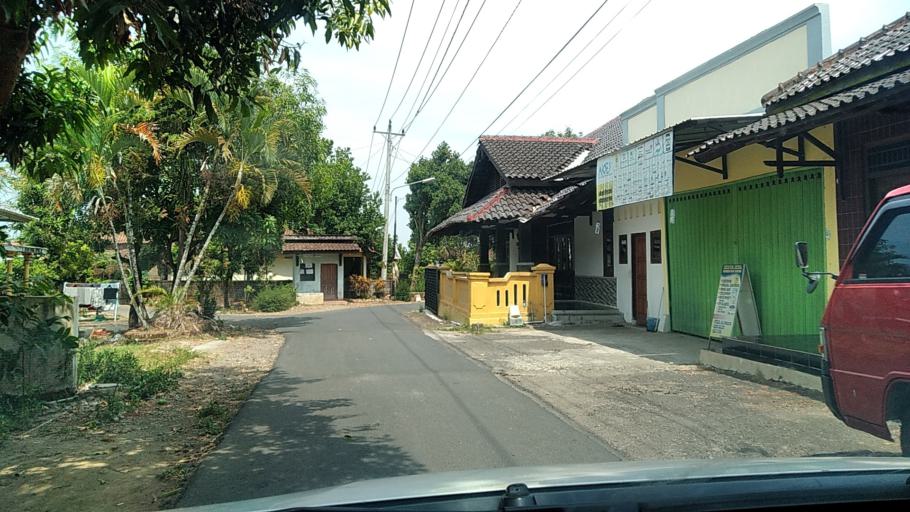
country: ID
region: Central Java
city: Ungaran
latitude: -7.0792
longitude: 110.3128
